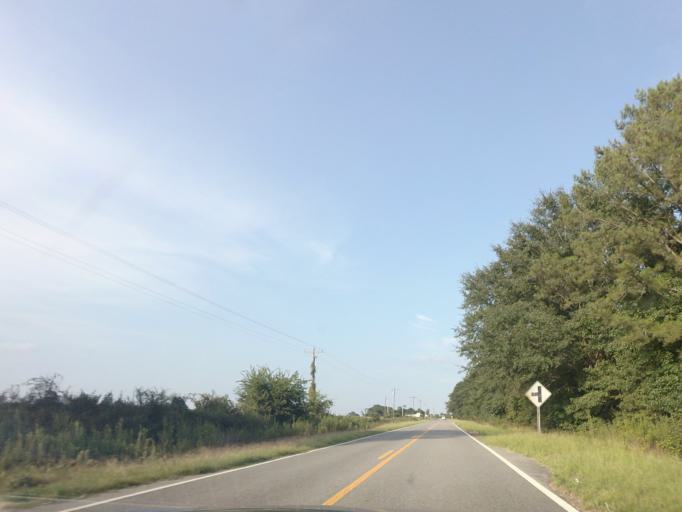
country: US
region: Georgia
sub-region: Bleckley County
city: Cochran
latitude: 32.4978
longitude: -83.2982
